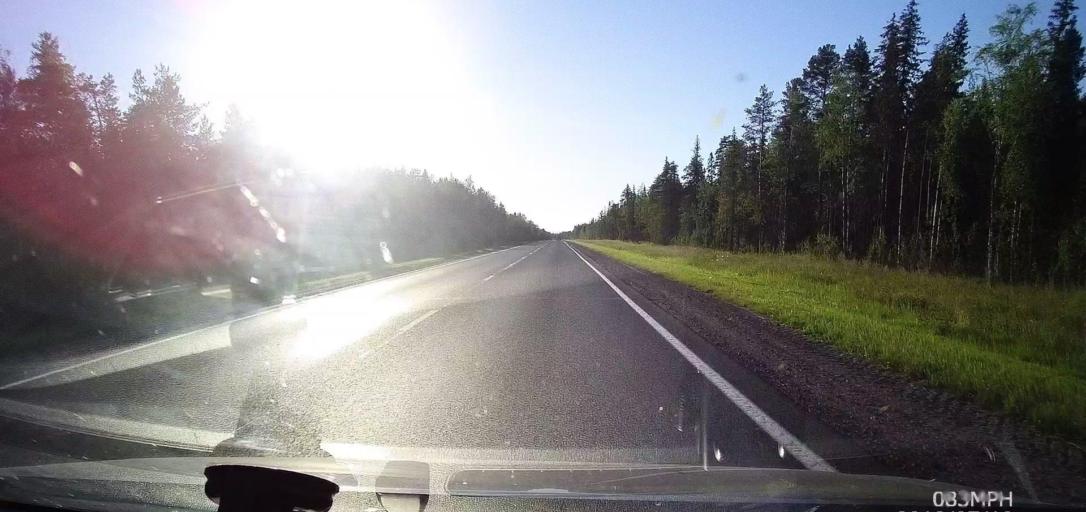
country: RU
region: Arkhangelskaya
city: Kholmogory
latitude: 64.1317
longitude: 41.6542
